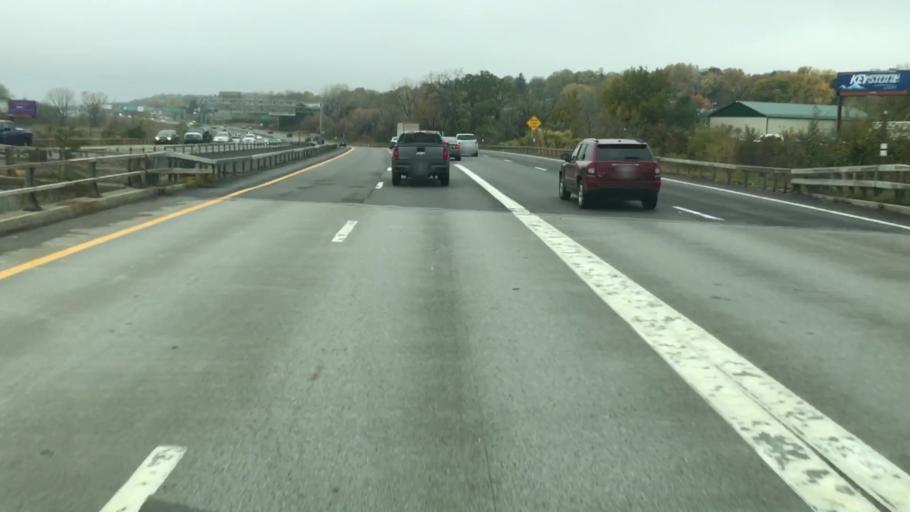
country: US
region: New York
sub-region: Onondaga County
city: East Syracuse
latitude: 43.0595
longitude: -76.0898
